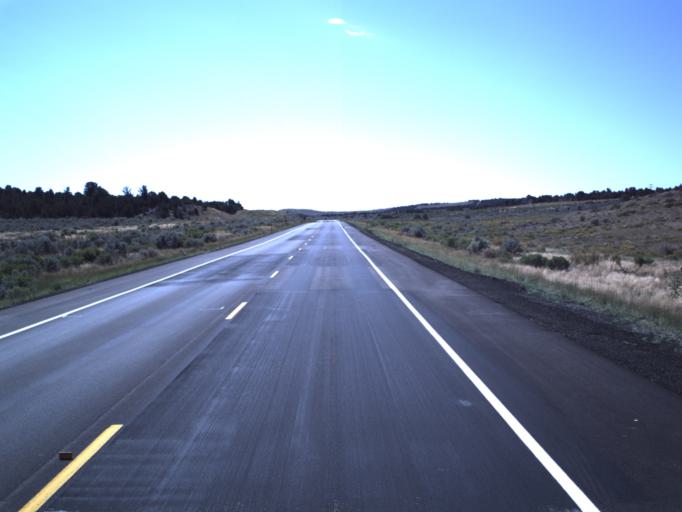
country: US
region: Utah
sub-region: Utah County
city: Genola
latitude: 39.9803
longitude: -112.2609
